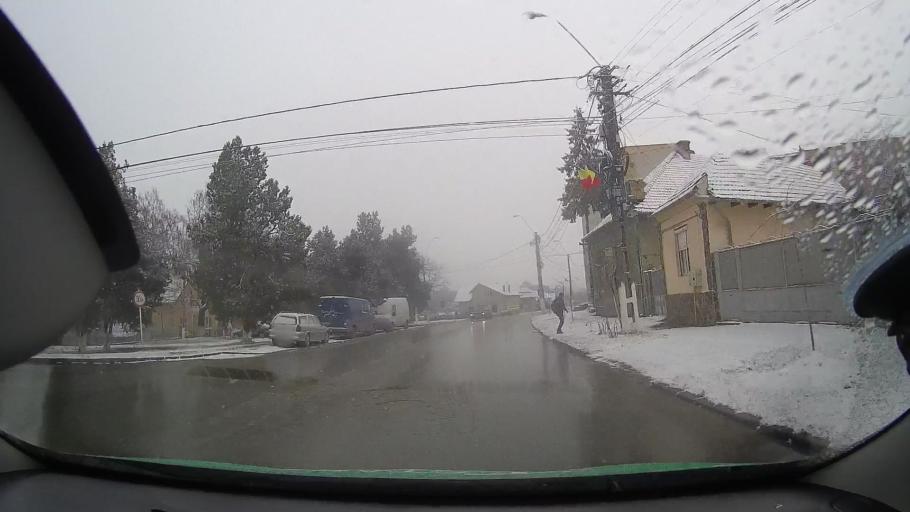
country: RO
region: Alba
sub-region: Municipiul Aiud
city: Aiud
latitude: 46.3108
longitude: 23.7317
